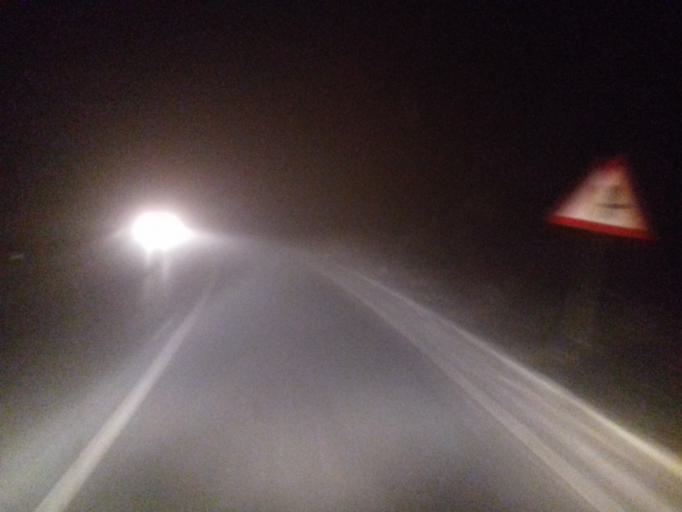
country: BA
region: Federation of Bosnia and Herzegovina
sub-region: Kanton Sarajevo
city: Sarajevo
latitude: 43.7986
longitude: 18.3558
